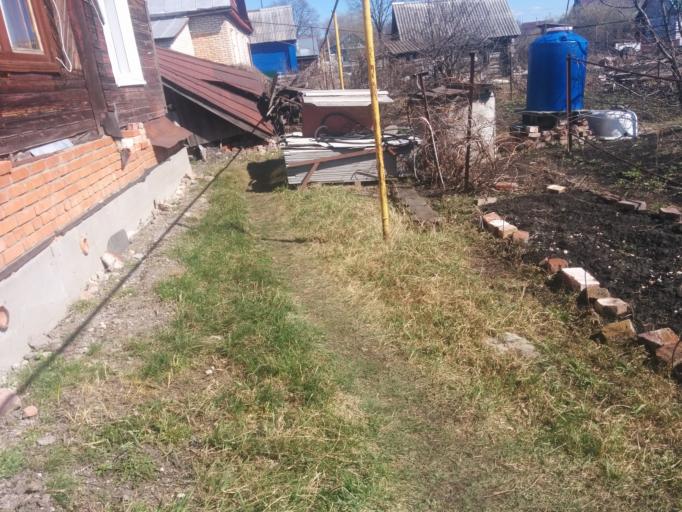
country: RU
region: Penza
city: Penza
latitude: 53.2005
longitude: 45.0601
